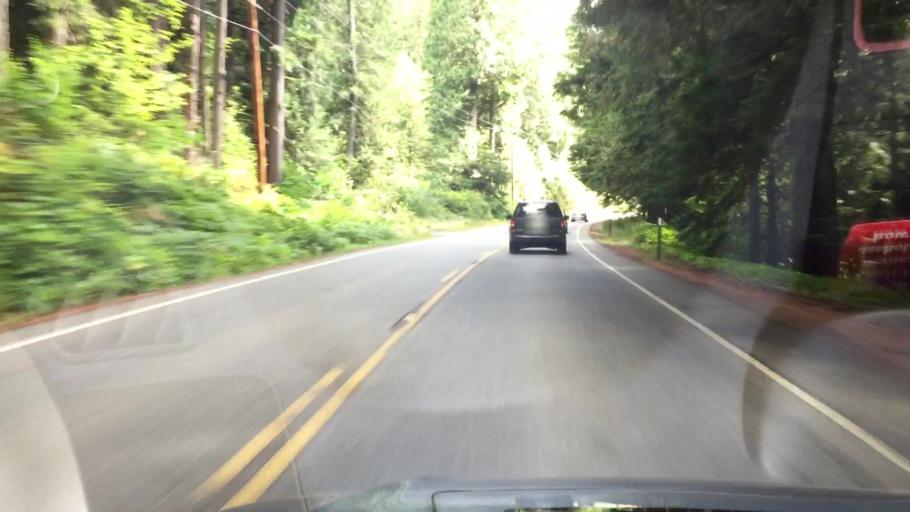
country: US
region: Washington
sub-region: Pierce County
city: Eatonville
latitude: 46.7471
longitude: -121.9247
